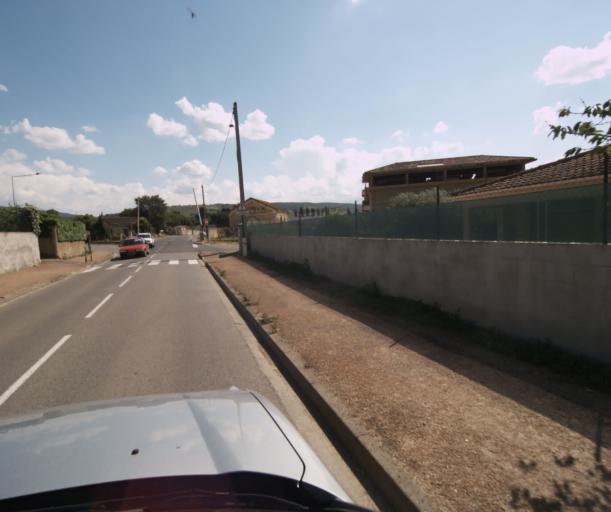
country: FR
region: Languedoc-Roussillon
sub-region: Departement de l'Aude
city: Limoux
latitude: 43.0622
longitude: 2.2225
